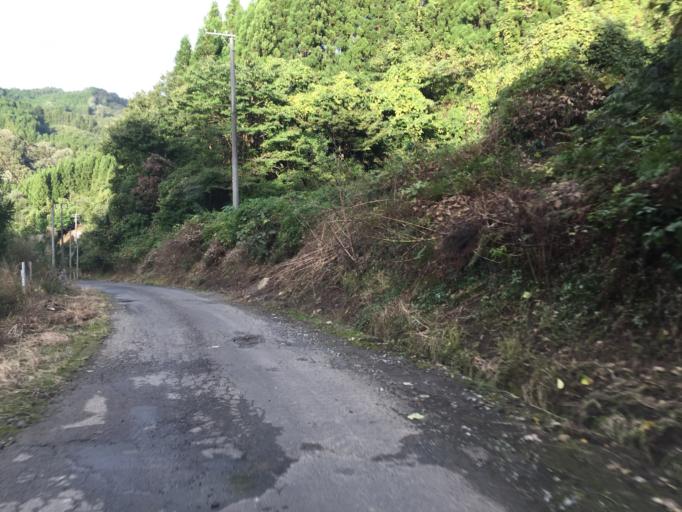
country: JP
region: Miyagi
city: Marumori
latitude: 37.9323
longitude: 140.7053
